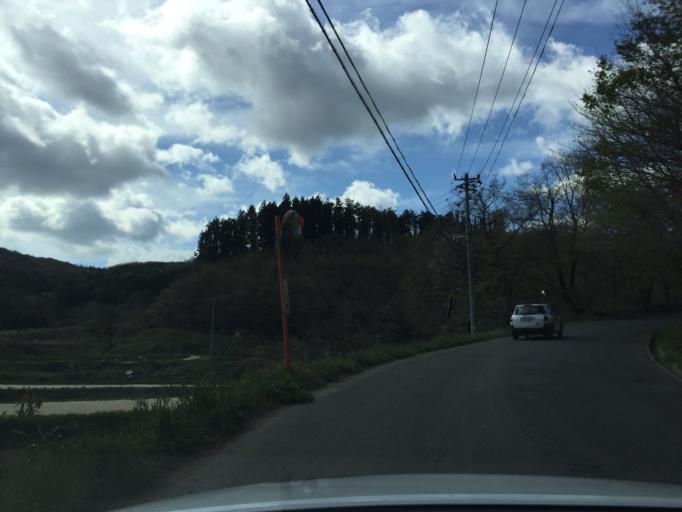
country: JP
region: Fukushima
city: Funehikimachi-funehiki
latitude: 37.5851
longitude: 140.6927
